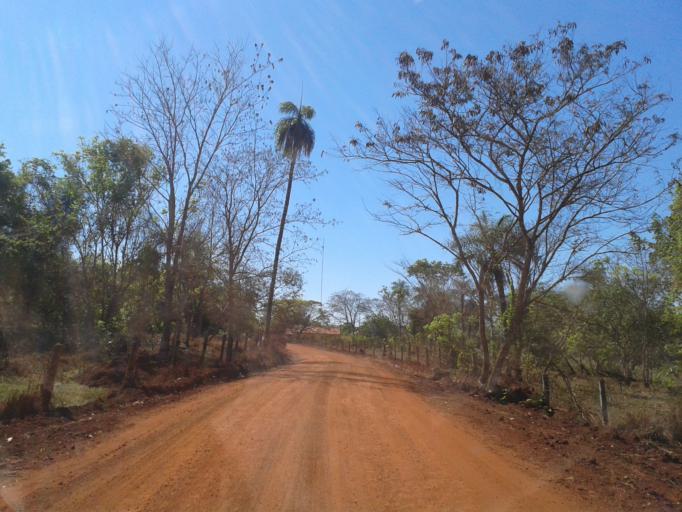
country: BR
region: Minas Gerais
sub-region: Ituiutaba
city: Ituiutaba
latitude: -19.0655
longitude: -49.3222
